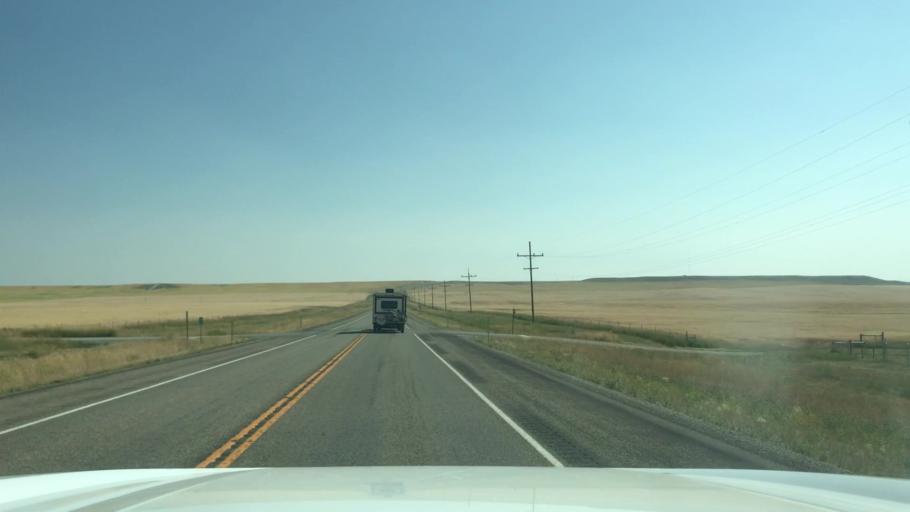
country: US
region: Montana
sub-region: Wheatland County
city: Harlowton
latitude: 46.4906
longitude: -109.7661
